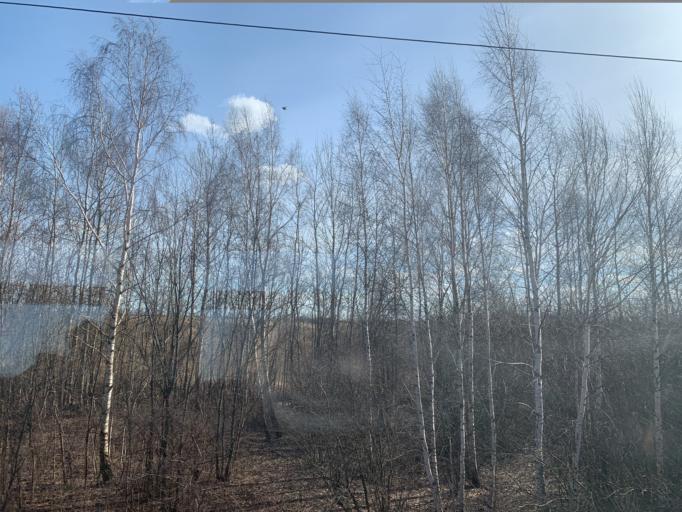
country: BY
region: Minsk
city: Stan'kava
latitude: 53.6884
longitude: 27.2255
